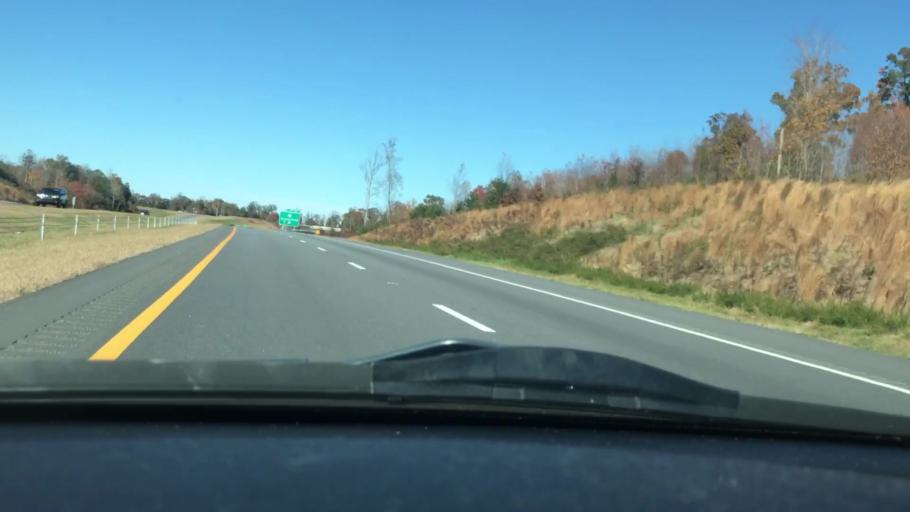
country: US
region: North Carolina
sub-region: Guilford County
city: Summerfield
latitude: 36.1945
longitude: -79.9289
